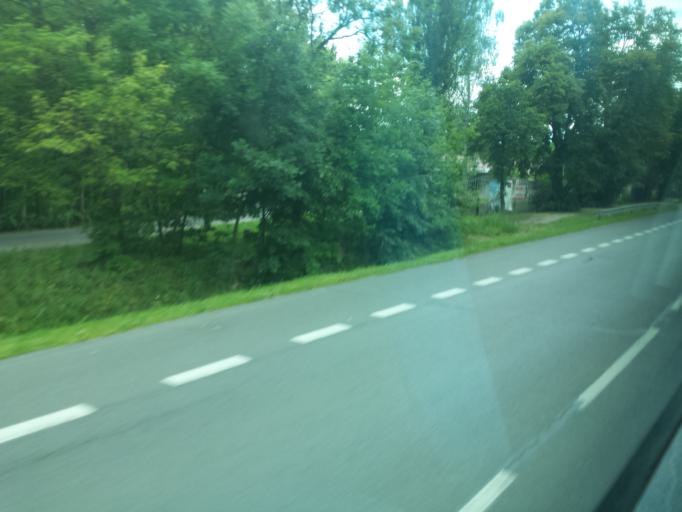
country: PL
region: Masovian Voivodeship
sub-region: Powiat minski
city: Sulejowek
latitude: 52.2213
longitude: 21.2512
